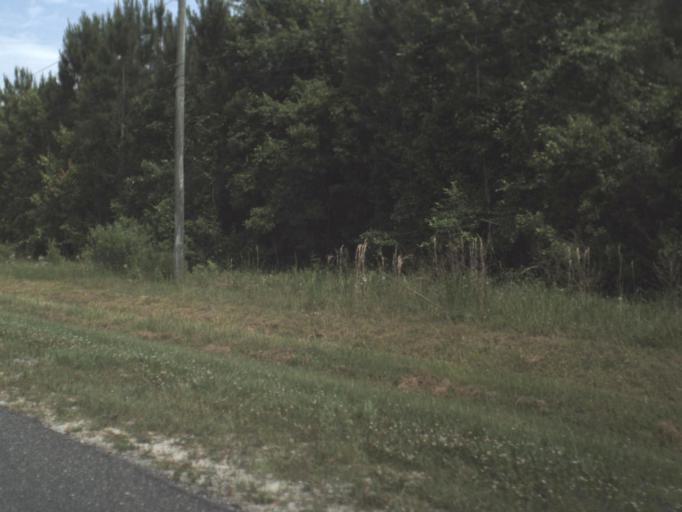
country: US
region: Florida
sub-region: Putnam County
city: Interlachen
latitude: 29.6264
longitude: -81.7883
